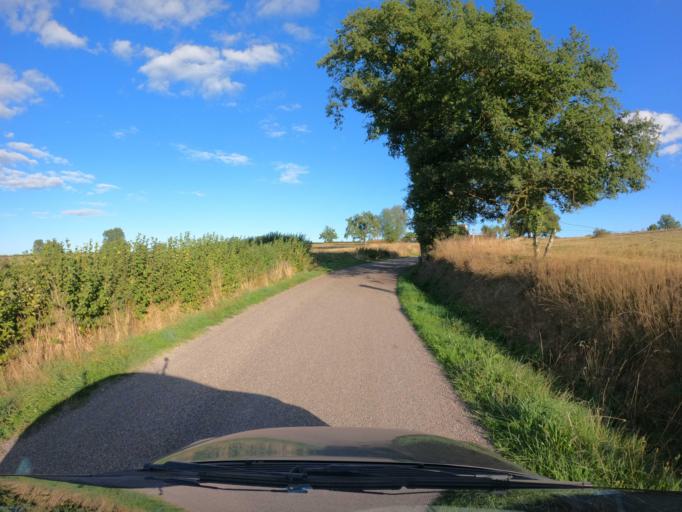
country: FR
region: Bourgogne
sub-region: Departement de Saone-et-Loire
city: Ecuisses
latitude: 46.7530
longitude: 4.5159
